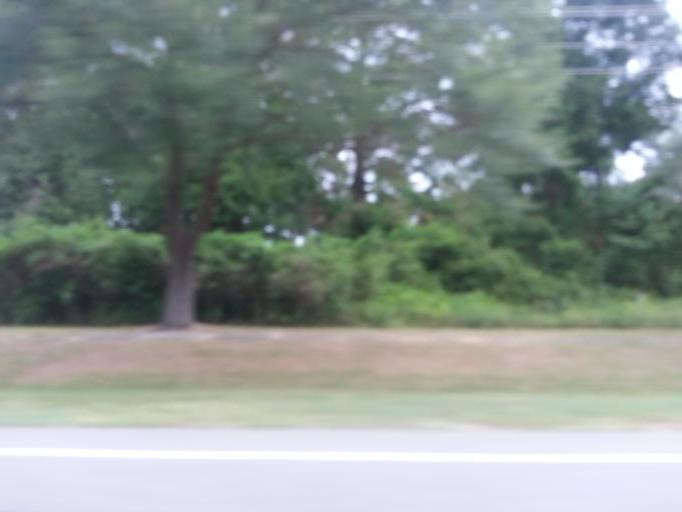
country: US
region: Alabama
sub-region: Baldwin County
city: Daphne
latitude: 30.6126
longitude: -87.9020
